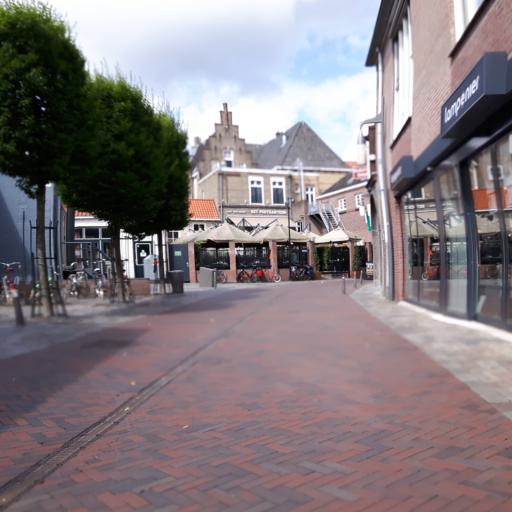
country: NL
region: Zeeland
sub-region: Gemeente Goes
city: Goes
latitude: 51.5048
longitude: 3.8917
